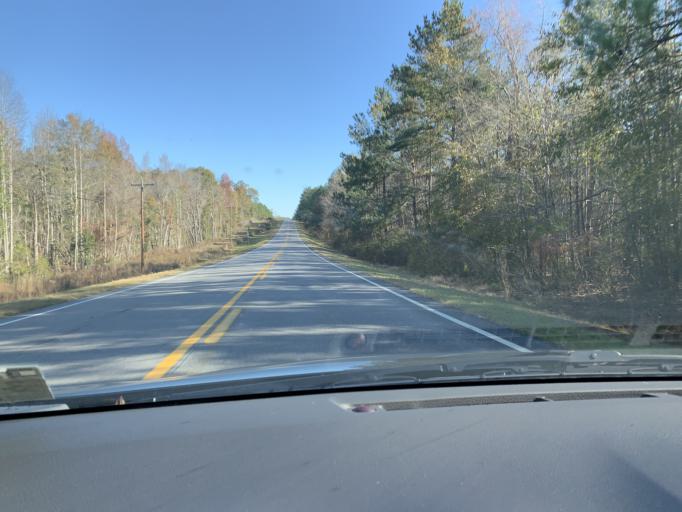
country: US
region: Georgia
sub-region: Ben Hill County
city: Fitzgerald
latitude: 31.7668
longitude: -83.1066
